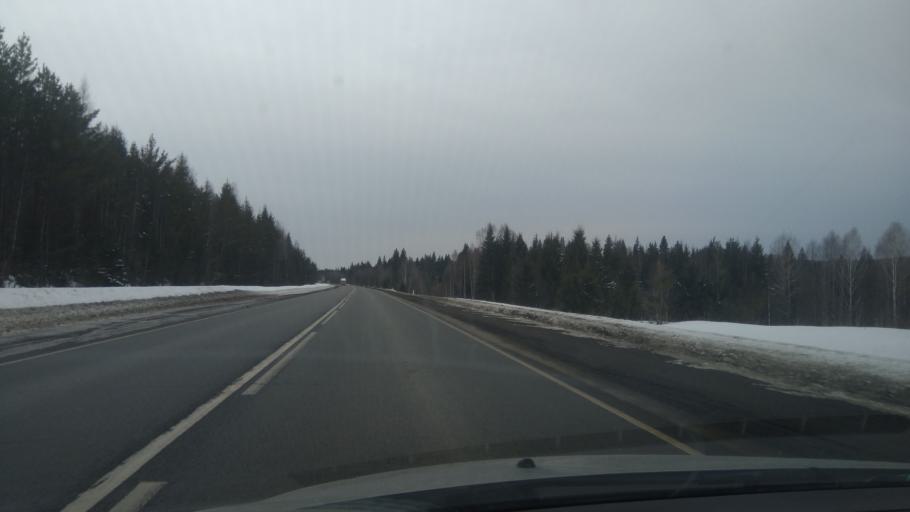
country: RU
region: Sverdlovsk
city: Arti
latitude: 56.7918
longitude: 58.4487
